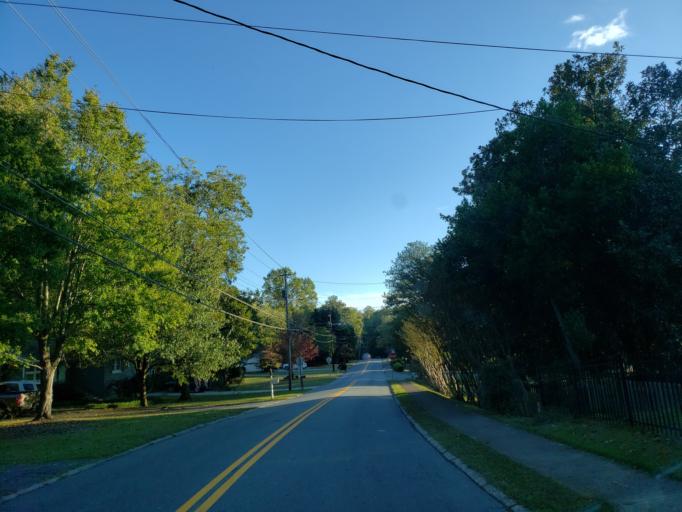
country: US
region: Georgia
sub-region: Cobb County
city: Marietta
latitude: 33.9472
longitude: -84.5690
